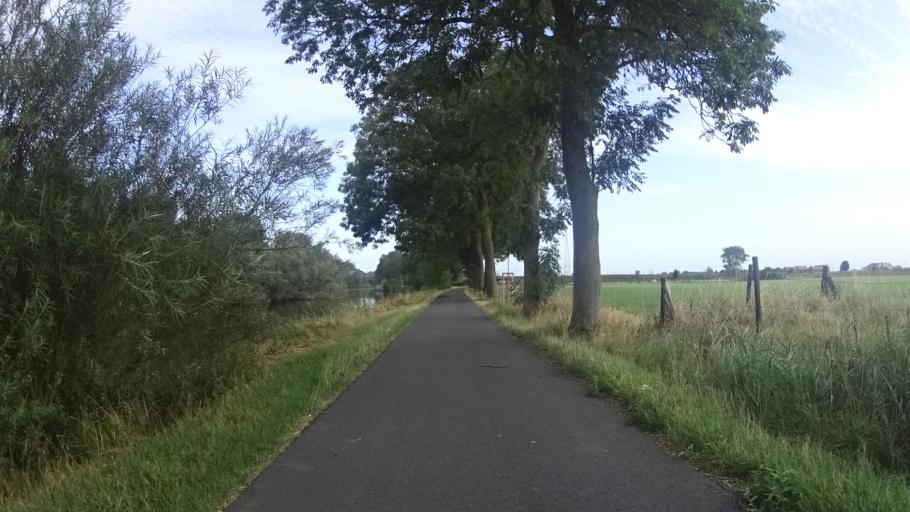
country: BE
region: Flanders
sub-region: Provincie West-Vlaanderen
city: Ieper
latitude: 50.9231
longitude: 2.8416
